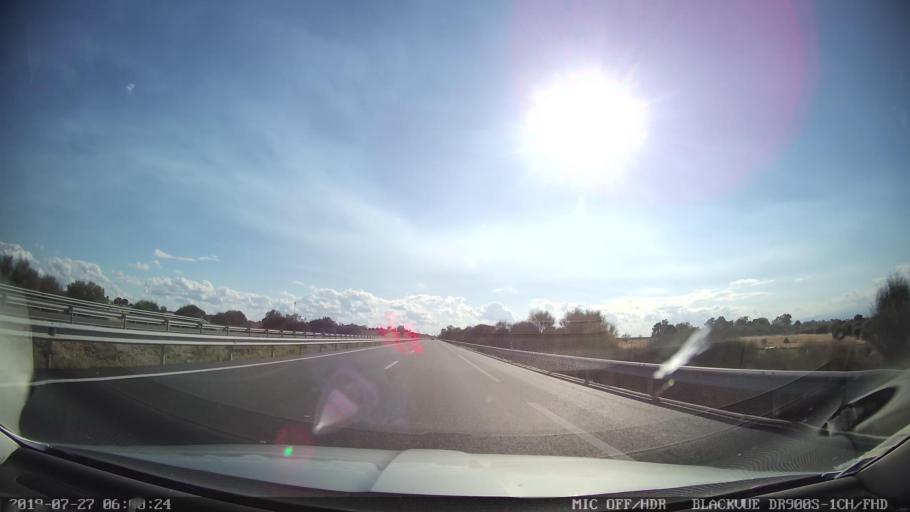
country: ES
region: Castille-La Mancha
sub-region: Province of Toledo
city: Caleruela
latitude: 39.8979
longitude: -5.2915
